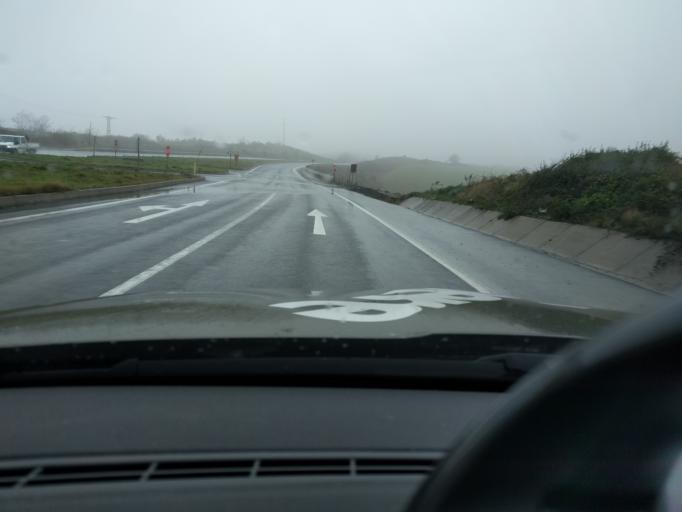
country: TR
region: Istanbul
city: Boyalik
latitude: 41.2802
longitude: 28.6321
